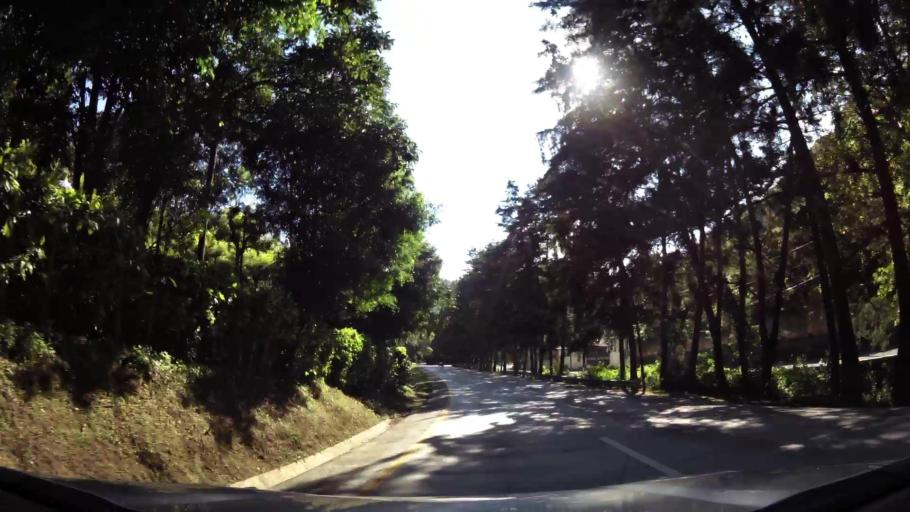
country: GT
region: Sacatepequez
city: Santa Lucia Milpas Altas
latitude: 14.5633
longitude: -90.7019
